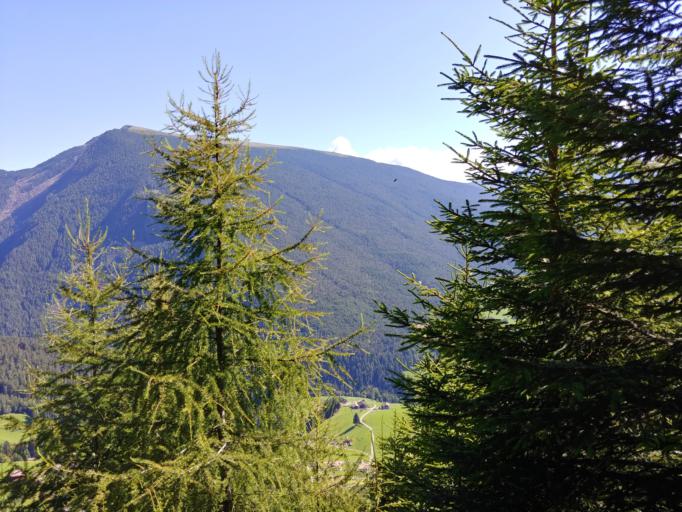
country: IT
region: Trentino-Alto Adige
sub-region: Bolzano
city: Ortisei
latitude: 46.5693
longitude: 11.6298
